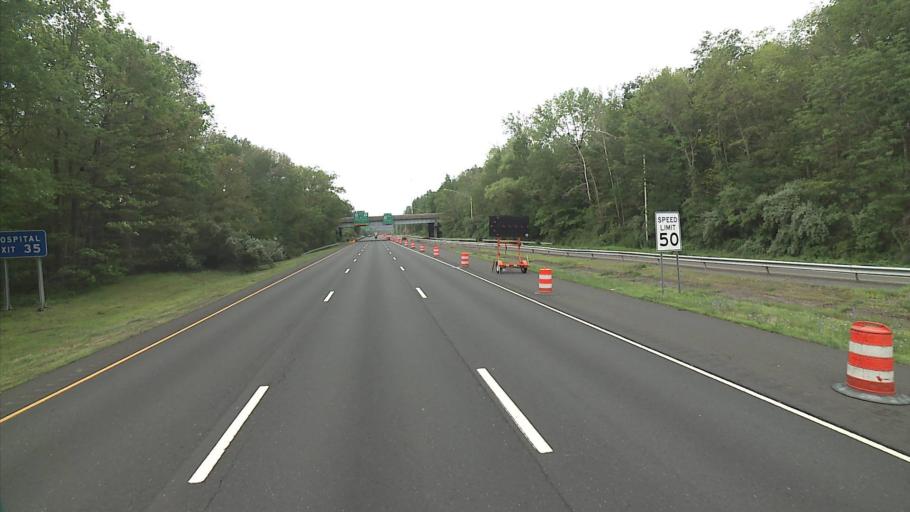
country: US
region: Connecticut
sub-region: Hartford County
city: Plainville
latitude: 41.6779
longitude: -72.8195
